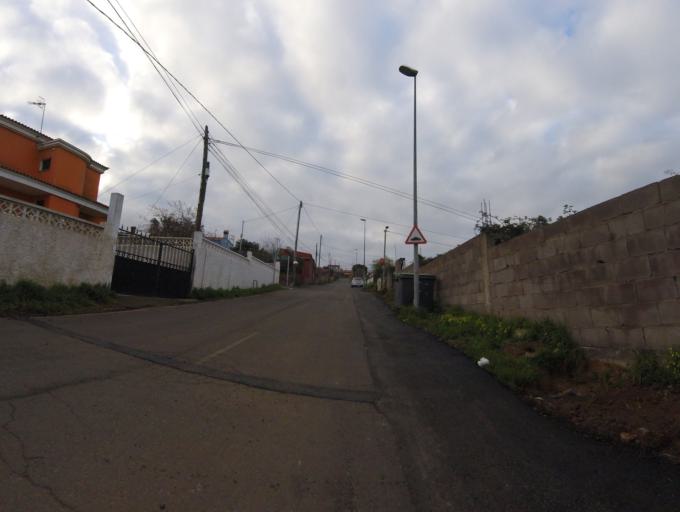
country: ES
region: Canary Islands
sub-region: Provincia de Santa Cruz de Tenerife
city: La Laguna
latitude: 28.4502
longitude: -16.3546
